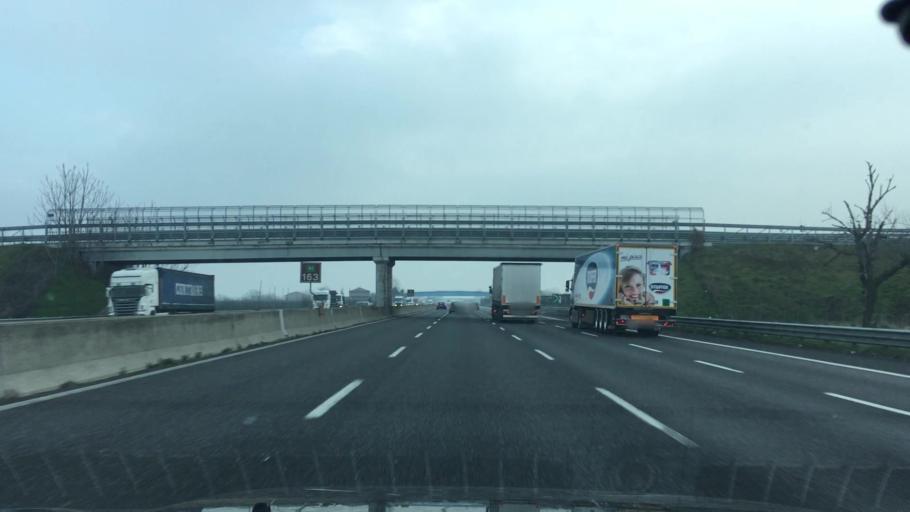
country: IT
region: Emilia-Romagna
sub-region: Provincia di Modena
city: Piumazzo
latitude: 44.5472
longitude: 11.0897
